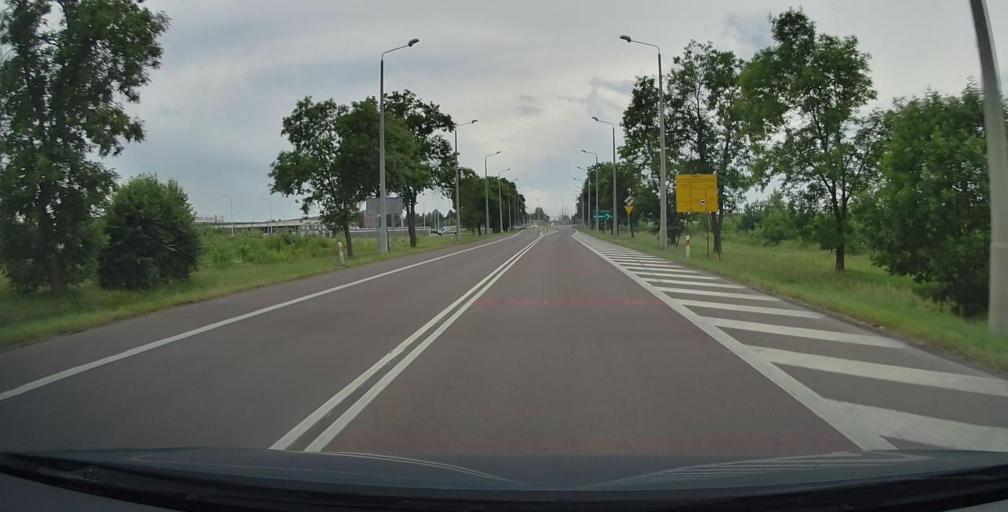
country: PL
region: Lublin Voivodeship
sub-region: Biala Podlaska
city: Biala Podlaska
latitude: 52.0396
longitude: 23.1911
